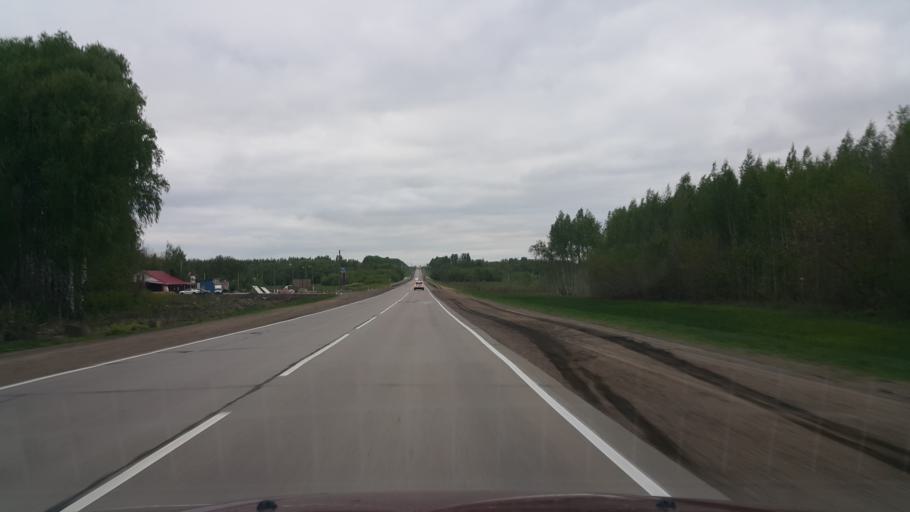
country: RU
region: Tambov
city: Znamenka
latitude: 52.3910
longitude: 41.4024
